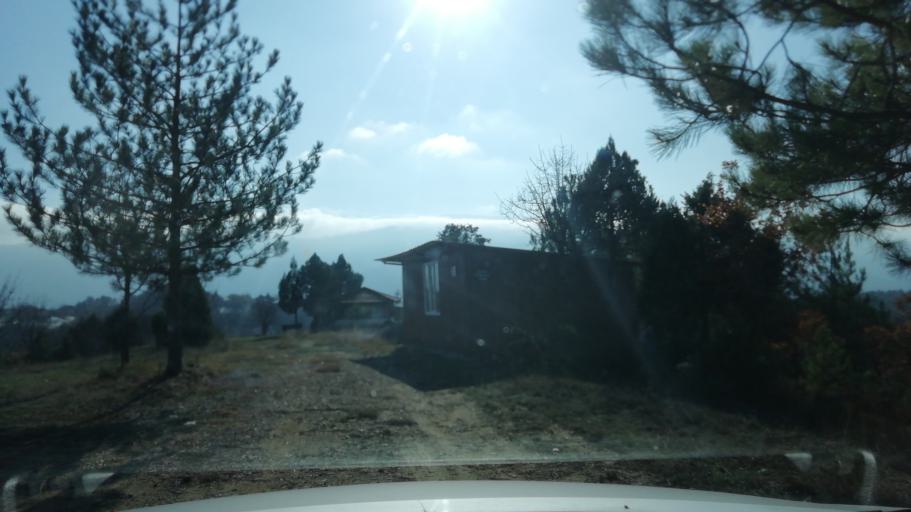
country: TR
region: Karabuk
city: Safranbolu
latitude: 41.2346
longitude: 32.7832
